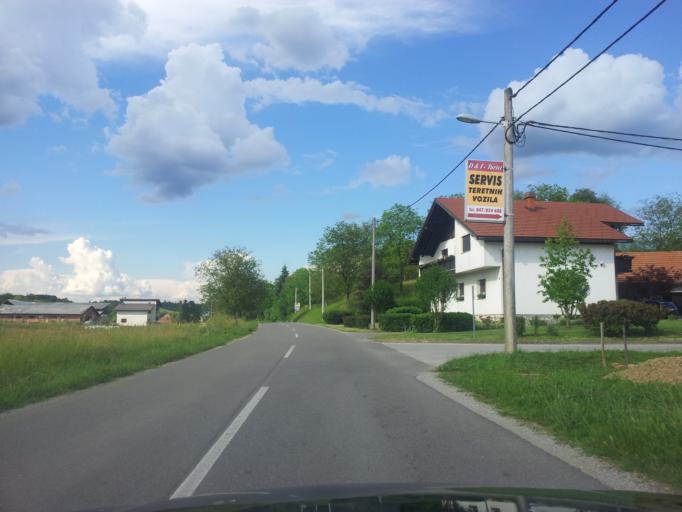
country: HR
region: Karlovacka
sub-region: Grad Karlovac
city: Karlovac
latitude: 45.4277
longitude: 15.4890
